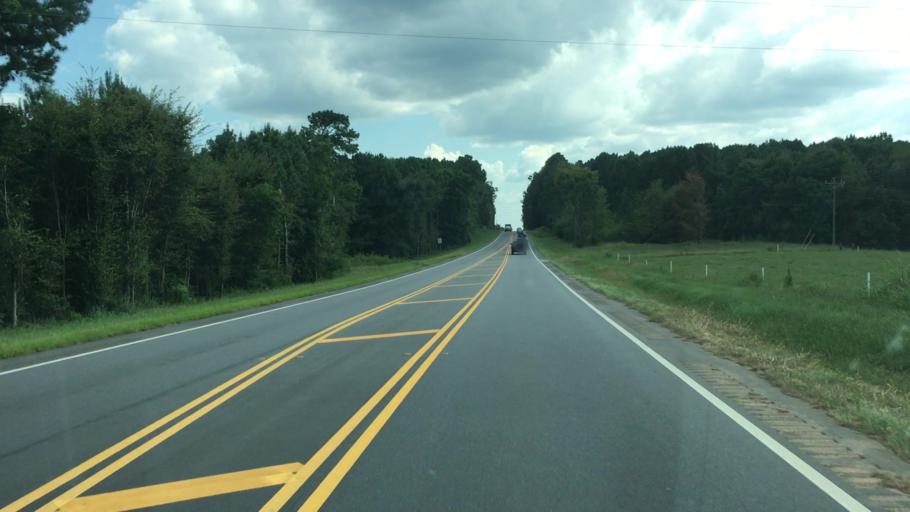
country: US
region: Georgia
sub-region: Putnam County
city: Jefferson
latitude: 33.4647
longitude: -83.4145
